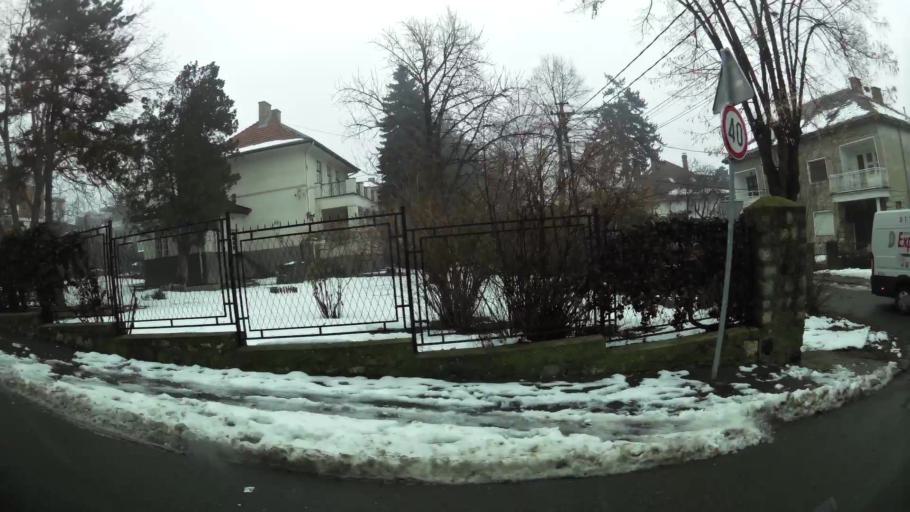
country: RS
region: Central Serbia
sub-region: Belgrade
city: Cukarica
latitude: 44.7863
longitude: 20.4357
